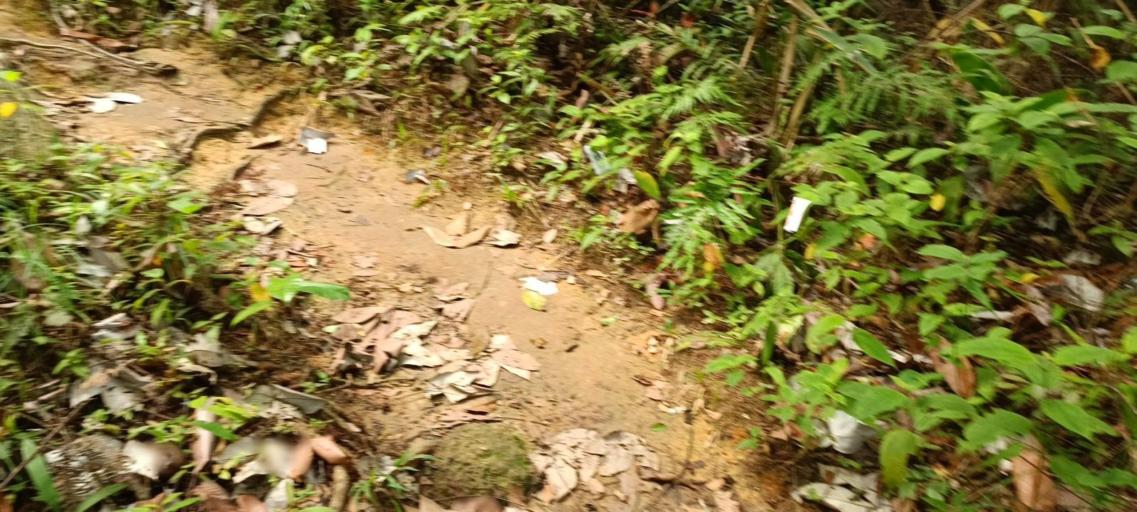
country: MY
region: Penang
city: Bukit Mertajam
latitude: 5.3739
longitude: 100.4819
